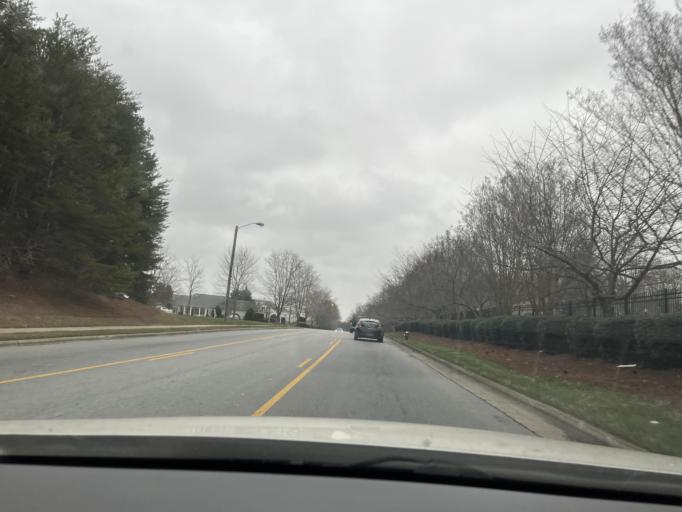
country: US
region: North Carolina
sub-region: Guilford County
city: Pleasant Garden
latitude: 36.0033
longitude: -79.8050
